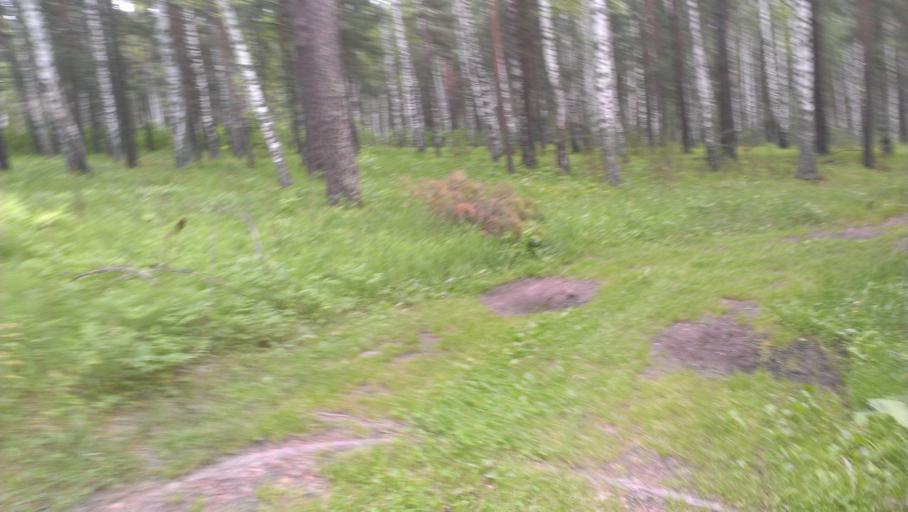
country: RU
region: Altai Krai
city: Sannikovo
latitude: 53.3421
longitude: 84.0462
